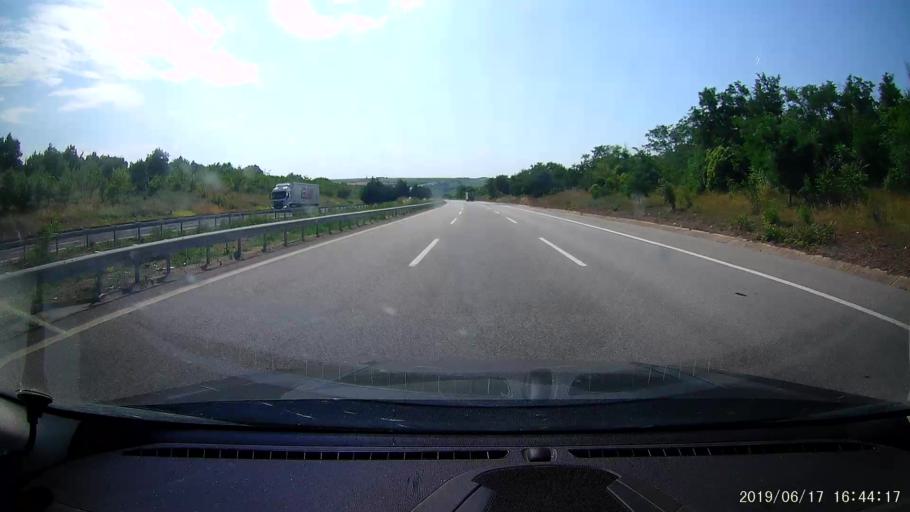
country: TR
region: Kirklareli
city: Luleburgaz
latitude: 41.4806
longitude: 27.2659
